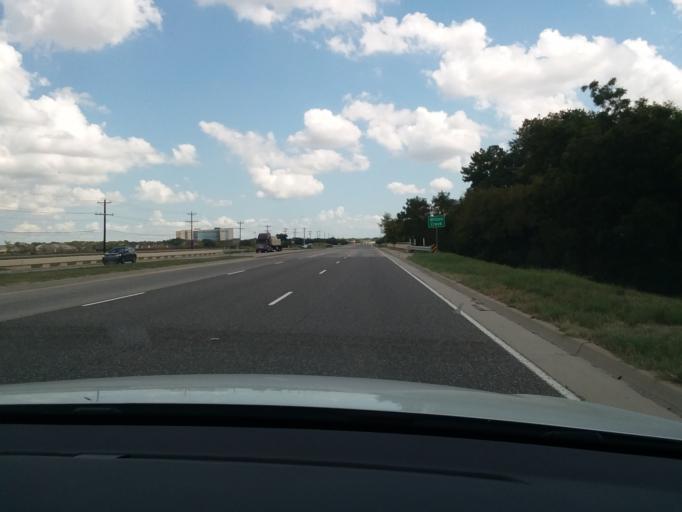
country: US
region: Texas
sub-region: Collin County
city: McKinney
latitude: 33.2181
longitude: -96.6949
